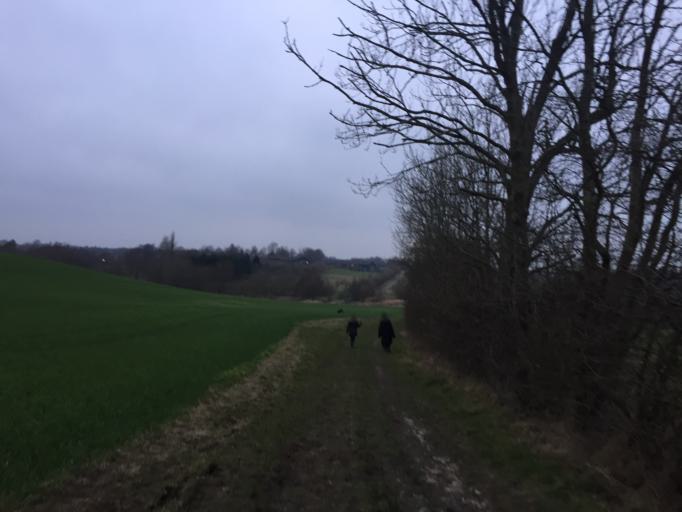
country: DK
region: South Denmark
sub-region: Kolding Kommune
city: Sonder Bjert
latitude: 55.4542
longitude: 9.5643
